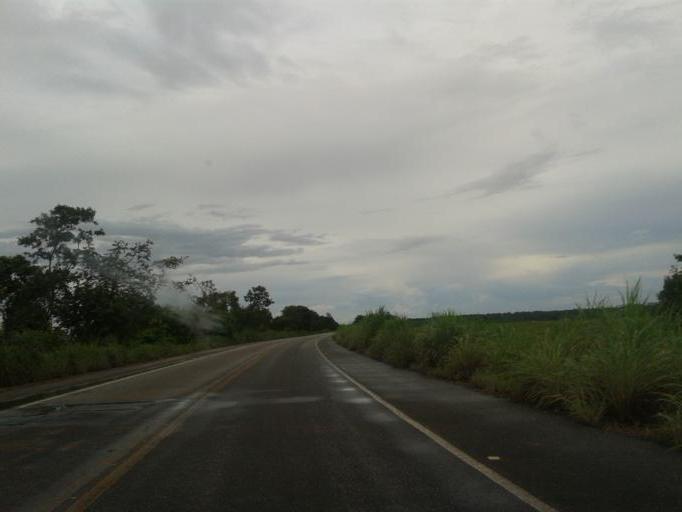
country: BR
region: Goias
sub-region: Mozarlandia
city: Mozarlandia
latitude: -14.8446
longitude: -50.5427
